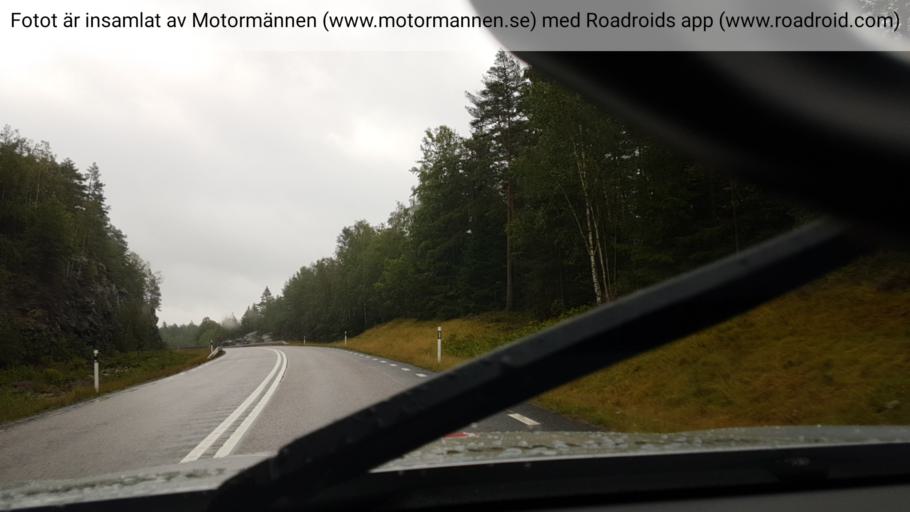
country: SE
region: Vaestra Goetaland
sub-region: Dals-Ed Kommun
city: Ed
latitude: 58.8729
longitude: 11.8469
